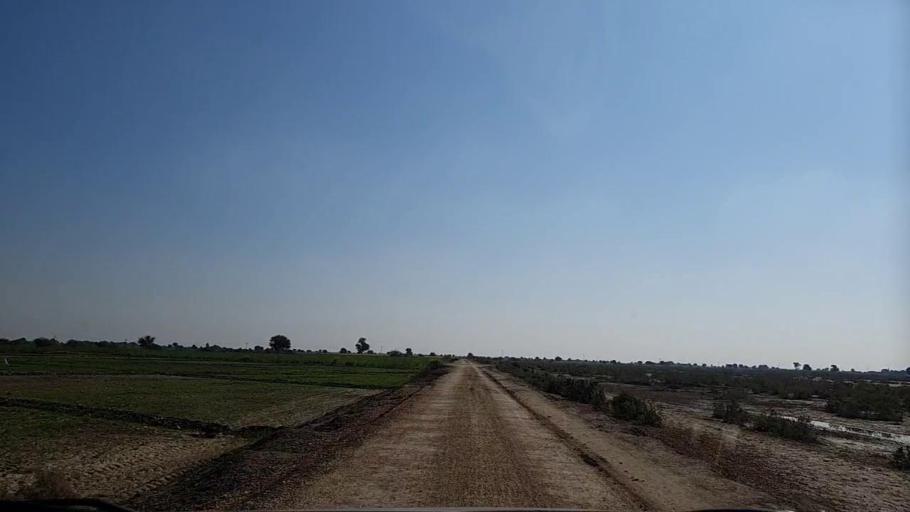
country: PK
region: Sindh
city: Pithoro
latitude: 25.6996
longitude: 69.3411
